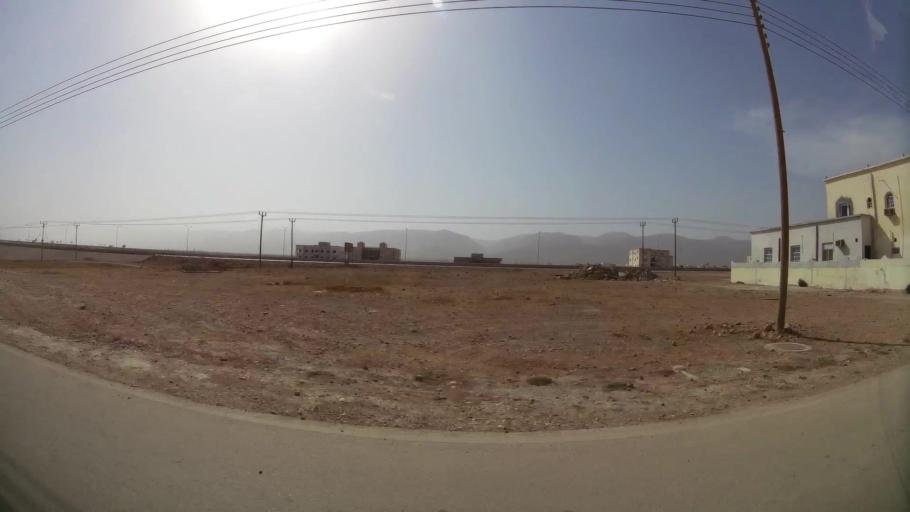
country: OM
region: Zufar
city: Salalah
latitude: 17.0092
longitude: 54.0012
